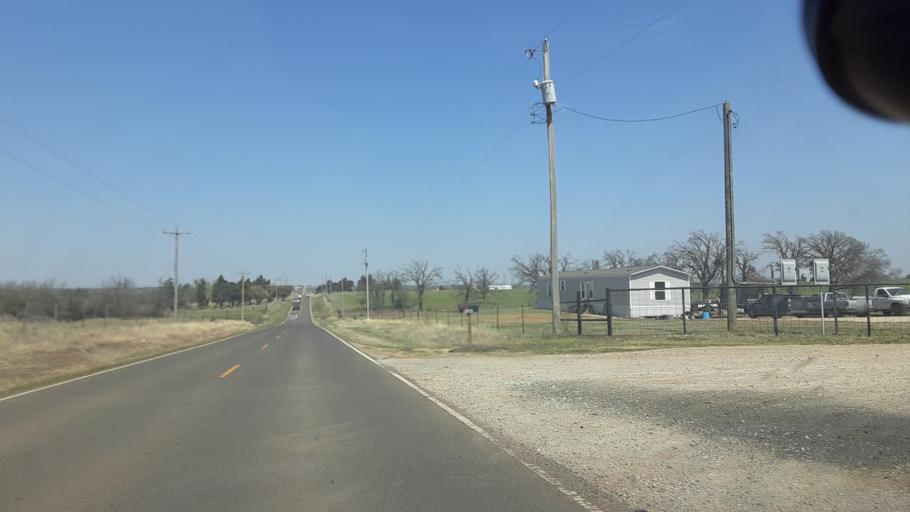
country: US
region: Oklahoma
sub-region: Logan County
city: Guthrie
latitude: 35.7941
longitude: -97.4783
